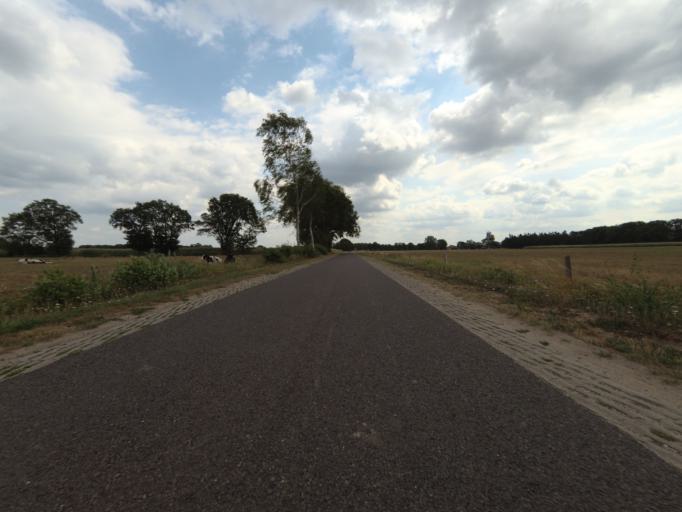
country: NL
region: Overijssel
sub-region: Gemeente Hof van Twente
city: Hengevelde
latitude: 52.1731
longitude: 6.6712
